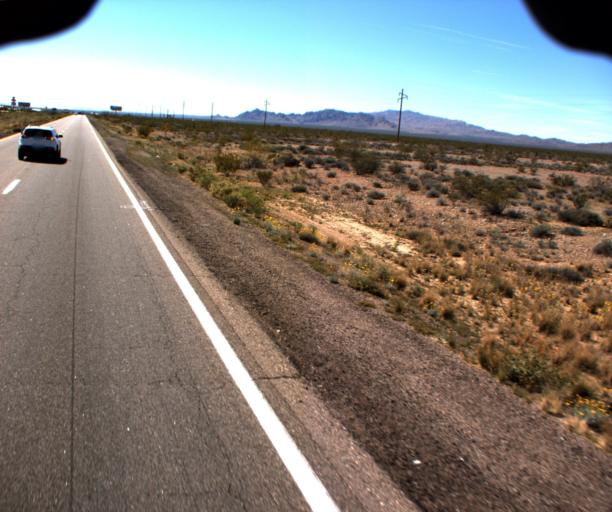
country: US
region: Arizona
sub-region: Mohave County
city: Dolan Springs
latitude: 35.7281
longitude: -114.4900
